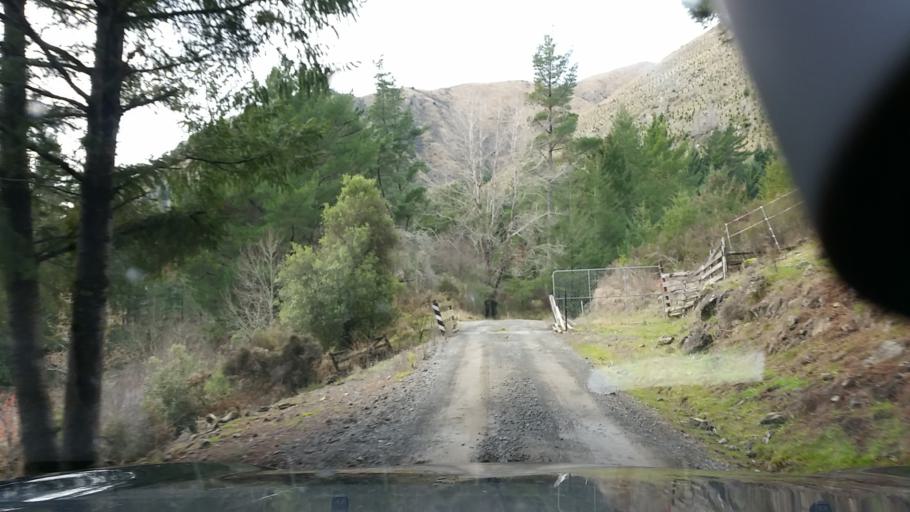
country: NZ
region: Tasman
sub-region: Tasman District
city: Richmond
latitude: -41.7301
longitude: 173.4675
